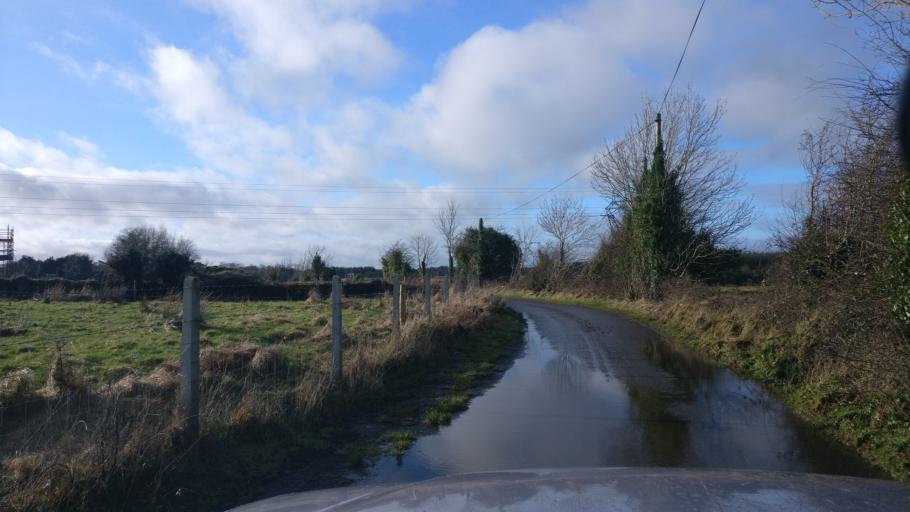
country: IE
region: Connaught
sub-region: County Galway
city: Loughrea
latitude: 53.2532
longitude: -8.6033
